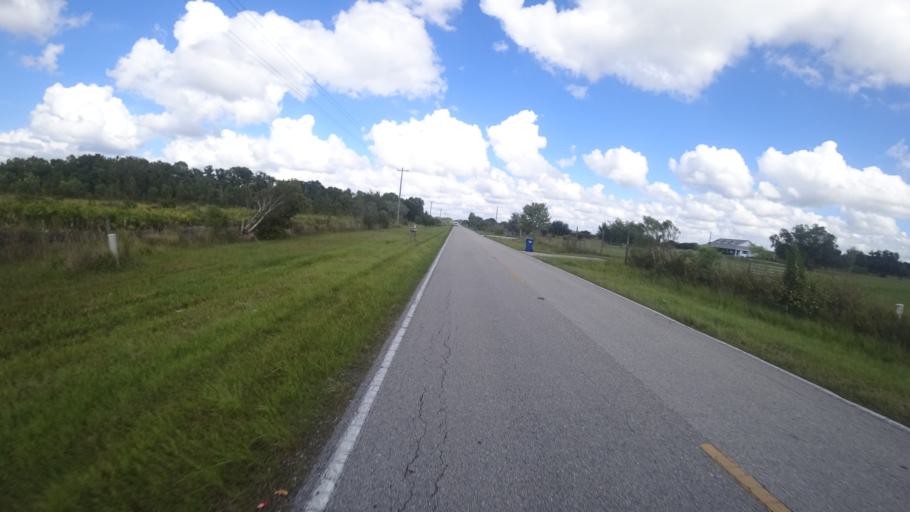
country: US
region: Florida
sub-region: Sarasota County
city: Lake Sarasota
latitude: 27.4131
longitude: -82.1334
